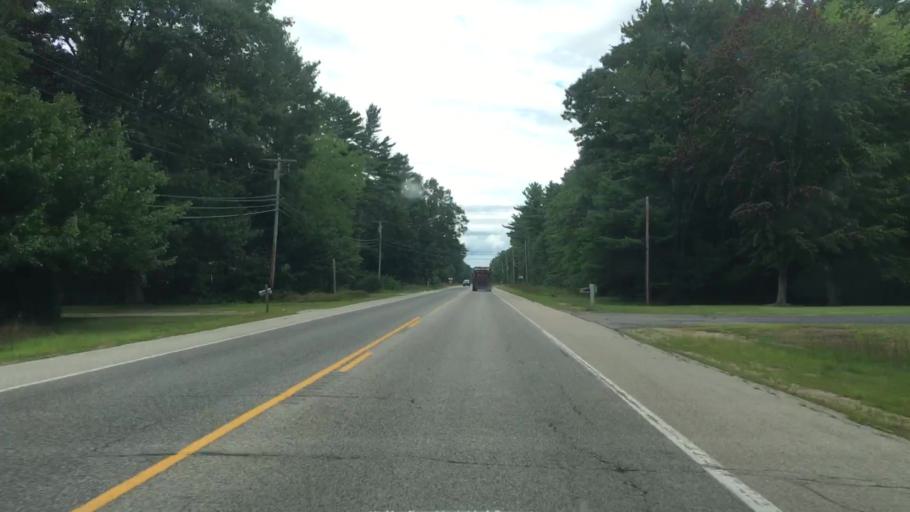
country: US
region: Maine
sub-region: York County
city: North Berwick
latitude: 43.3358
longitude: -70.7338
